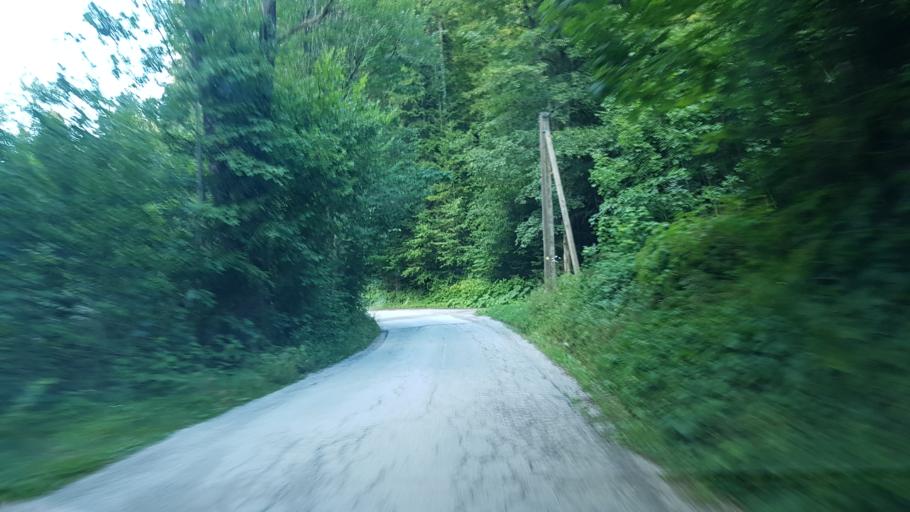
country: SI
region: Idrija
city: Spodnja Idrija
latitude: 46.0833
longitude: 14.0351
